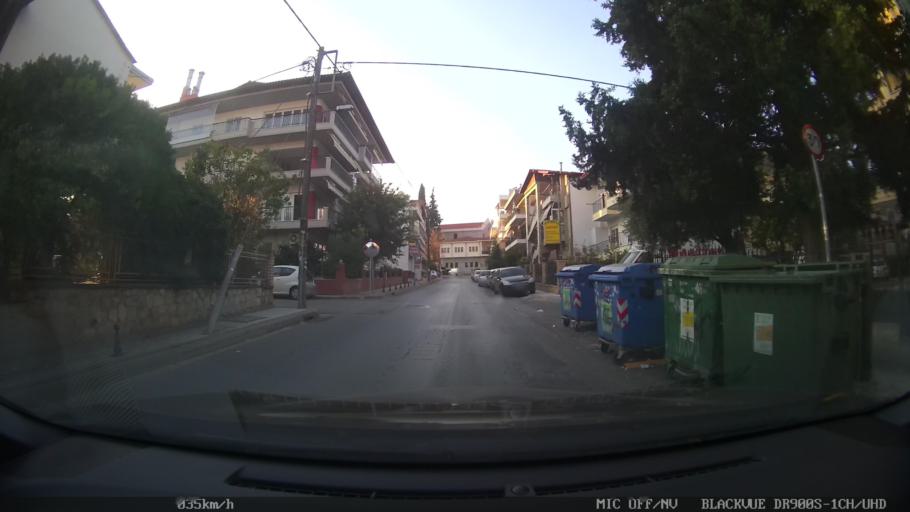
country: GR
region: Central Macedonia
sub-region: Nomos Thessalonikis
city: Pylaia
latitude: 40.6021
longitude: 22.9897
